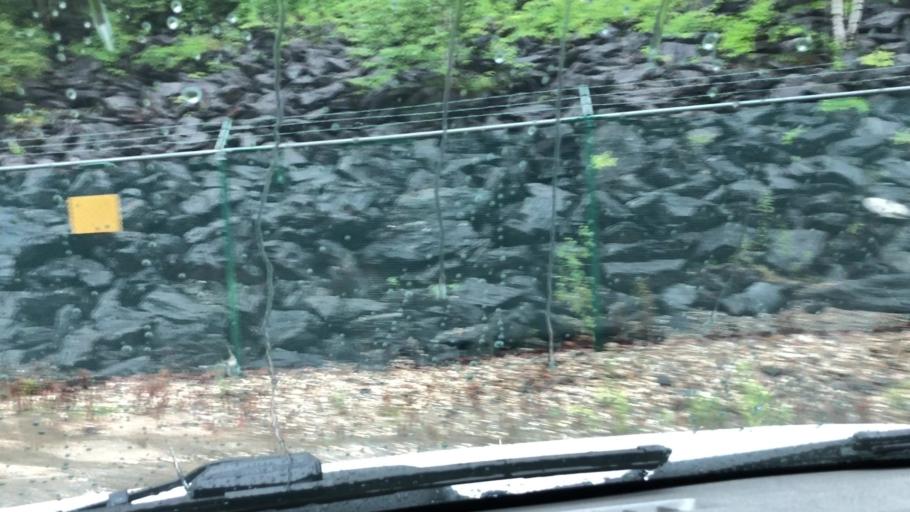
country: US
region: Massachusetts
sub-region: Berkshire County
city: Pittsfield
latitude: 42.4187
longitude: -73.2808
